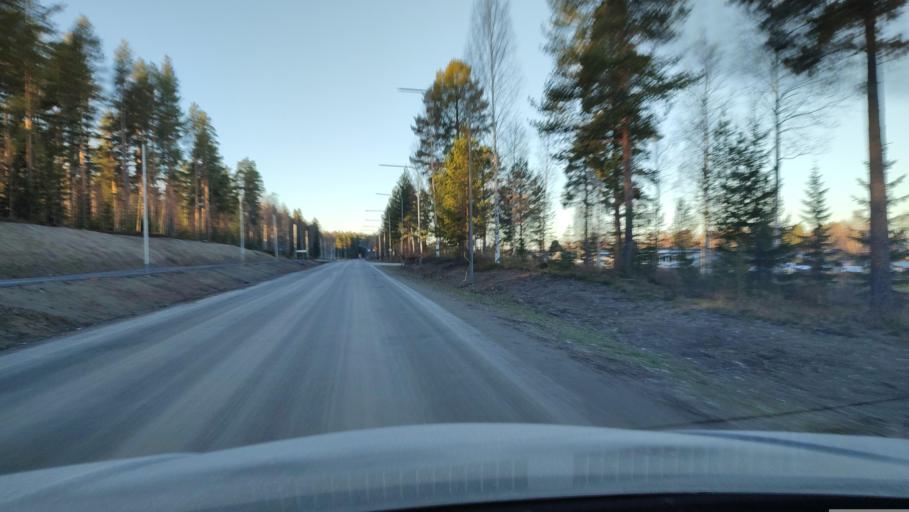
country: SE
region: Vaesterbotten
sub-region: Skelleftea Kommun
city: Skelleftea
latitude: 64.7397
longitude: 20.9372
